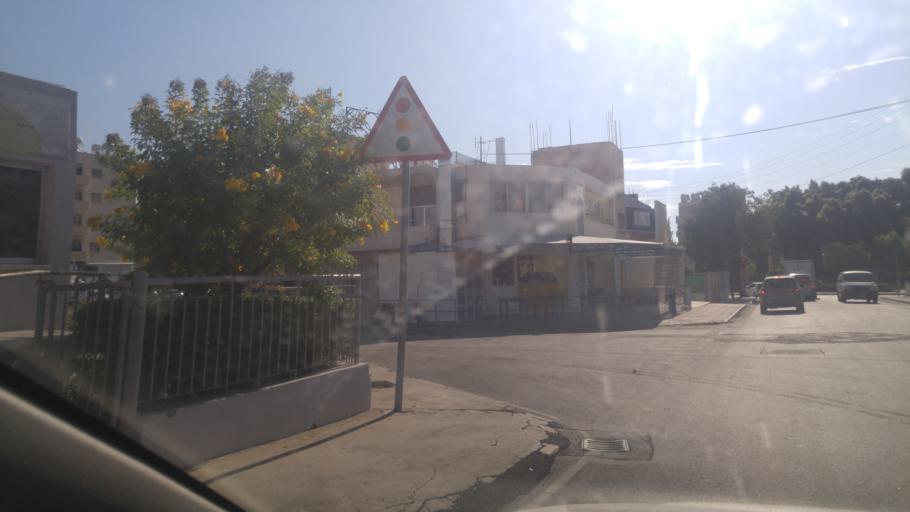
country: CY
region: Limassol
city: Limassol
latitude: 34.6902
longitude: 33.0580
